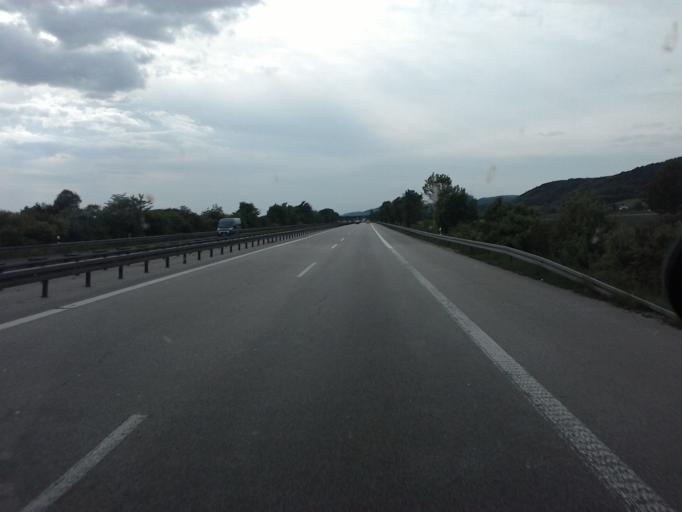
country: DE
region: Bavaria
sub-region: Lower Bavaria
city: Kirchroth
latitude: 48.9666
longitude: 12.5175
